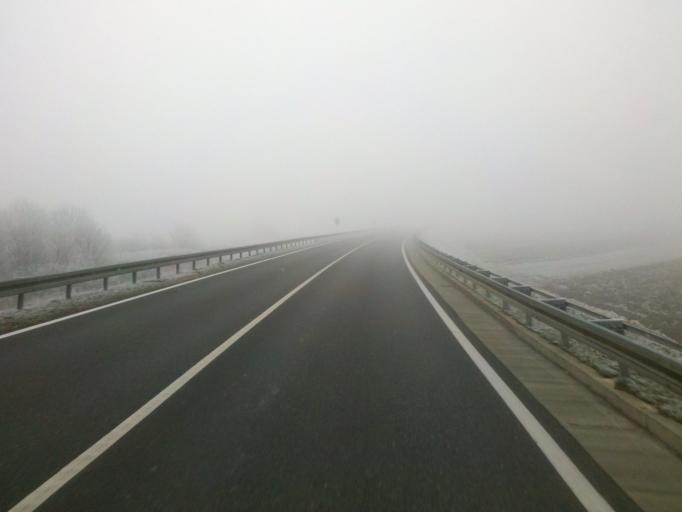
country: HR
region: Varazdinska
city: Jalkovec
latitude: 46.2905
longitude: 16.3099
